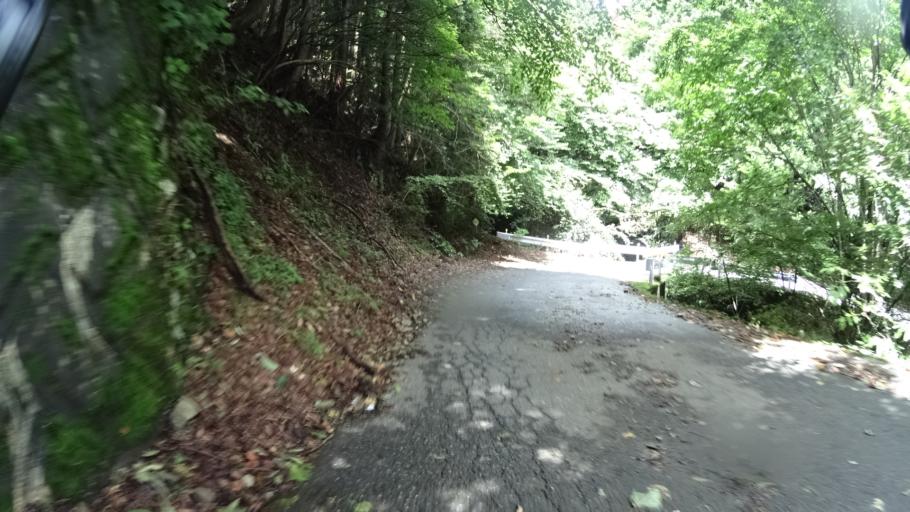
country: JP
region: Saitama
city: Chichibu
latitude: 35.8918
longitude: 139.1320
